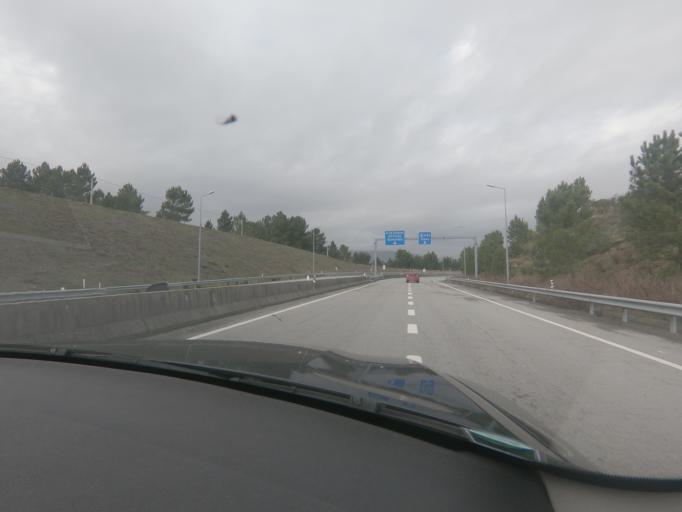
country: PT
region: Vila Real
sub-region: Vila Real
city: Vila Real
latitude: 41.3250
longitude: -7.7009
